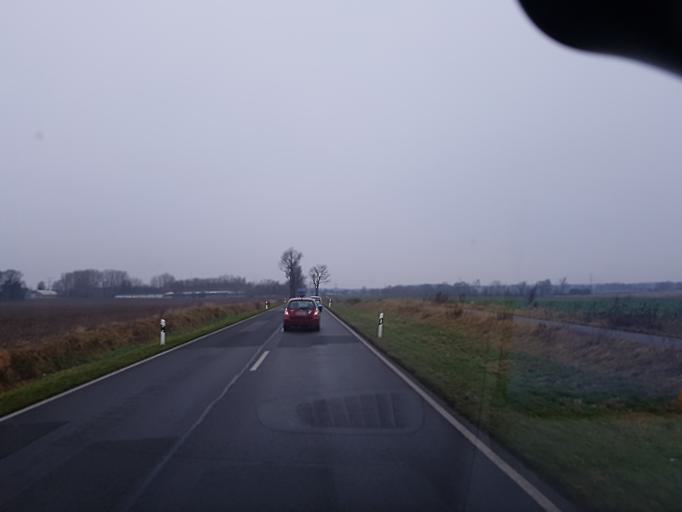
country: DE
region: Brandenburg
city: Lubbenau
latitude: 51.8718
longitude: 13.9151
